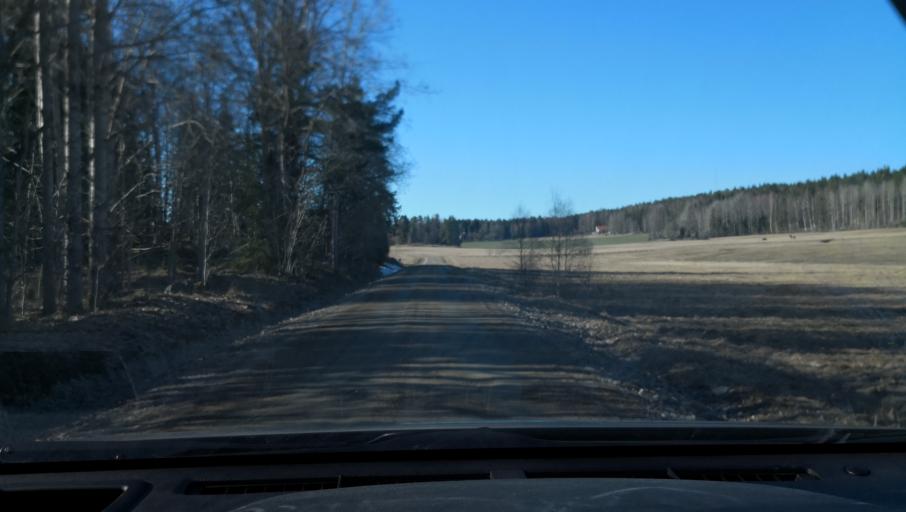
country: SE
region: Vaestmanland
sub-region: Sala Kommun
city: Sala
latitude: 60.1471
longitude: 16.6419
